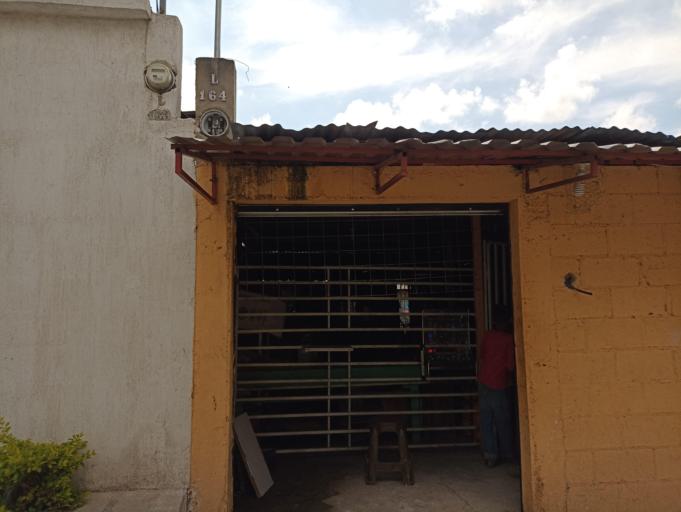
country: GT
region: Guatemala
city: Villa Canales
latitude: 14.4894
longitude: -90.5383
